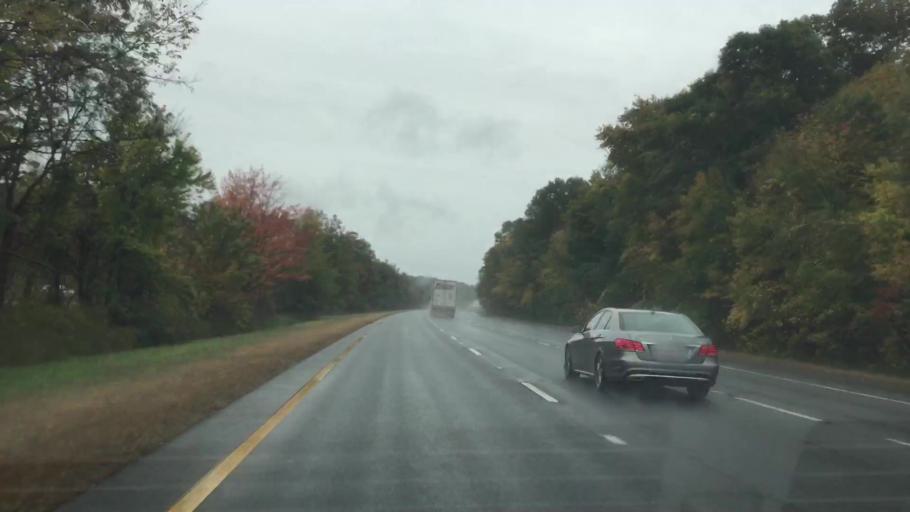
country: US
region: Massachusetts
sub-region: Essex County
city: Merrimac
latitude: 42.8259
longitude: -71.0053
